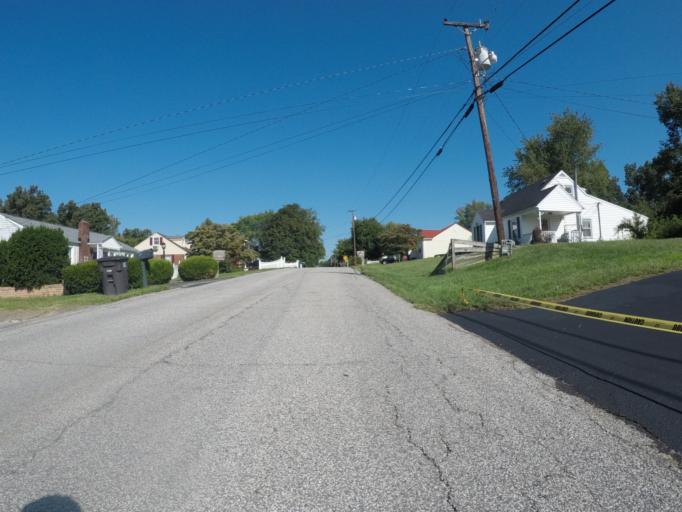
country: US
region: Kentucky
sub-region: Boyd County
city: Westwood
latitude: 38.4861
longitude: -82.6877
